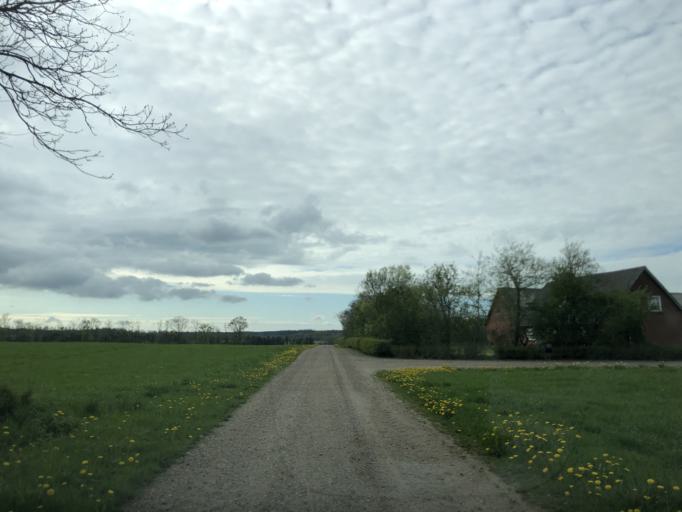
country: DK
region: Central Jutland
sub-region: Holstebro Kommune
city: Ulfborg
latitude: 56.1919
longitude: 8.4714
